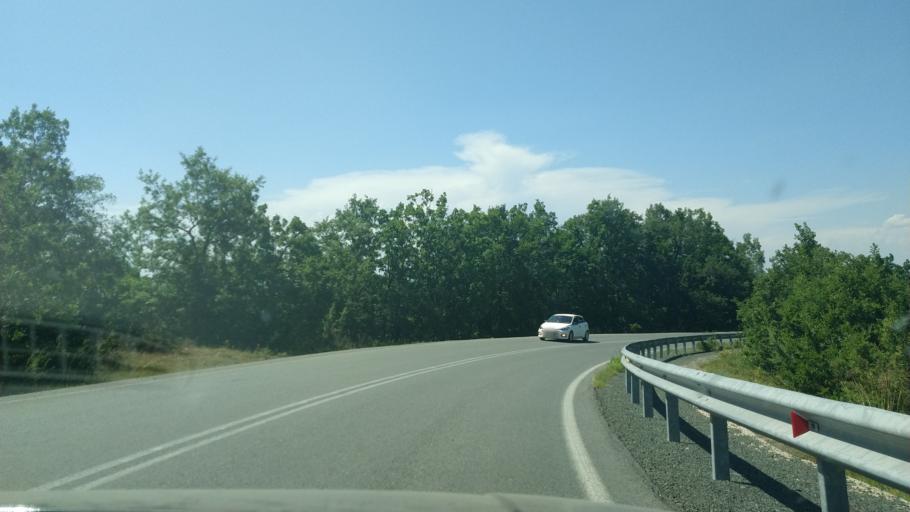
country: GR
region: West Macedonia
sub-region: Nomos Grevenon
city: Grevena
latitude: 40.0218
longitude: 21.4845
